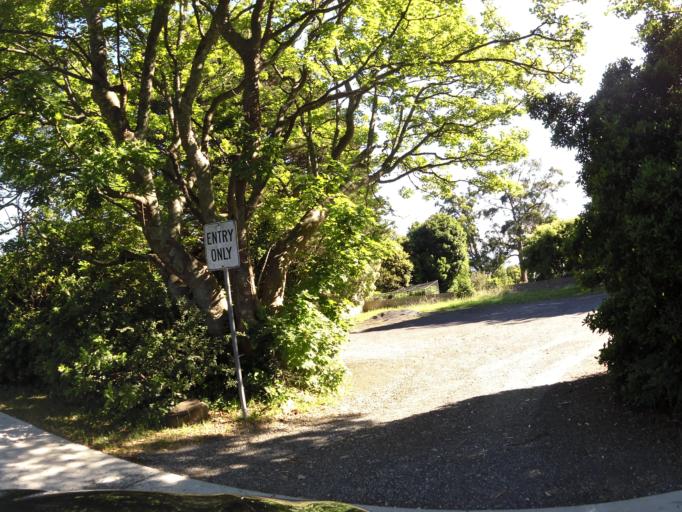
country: AU
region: Victoria
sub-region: Yarra Ranges
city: Ferny Creek
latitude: -37.8844
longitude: 145.3348
